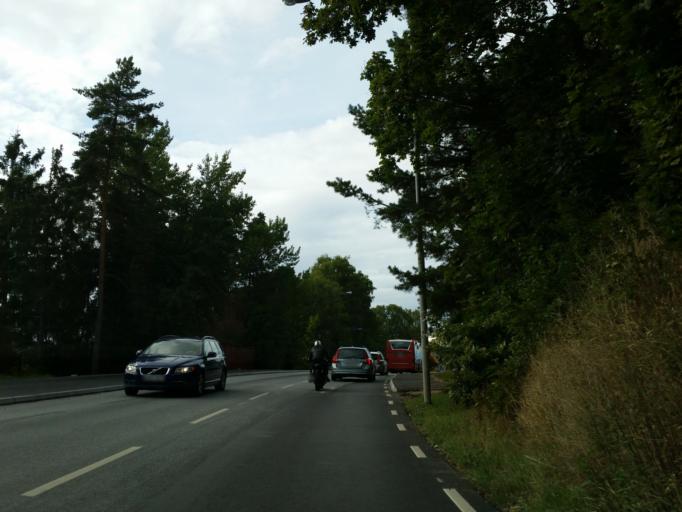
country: SE
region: Stockholm
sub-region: Sollentuna Kommun
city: Sollentuna
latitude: 59.4432
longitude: 17.9469
